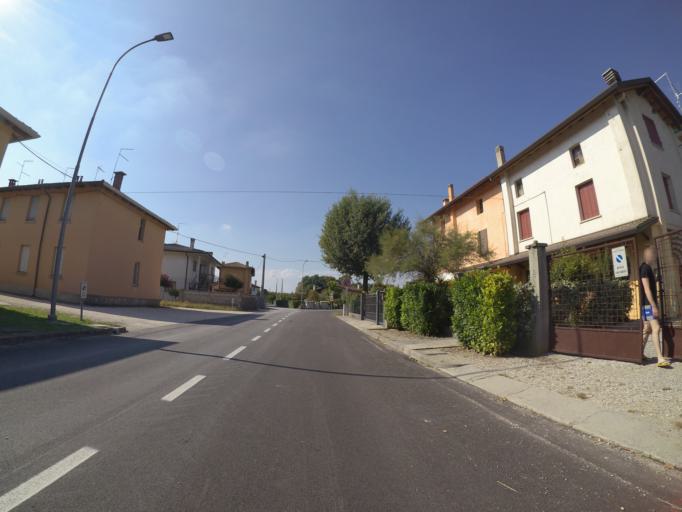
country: IT
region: Friuli Venezia Giulia
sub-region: Provincia di Udine
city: Muzzana del Turgnano
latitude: 45.8171
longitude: 13.1192
